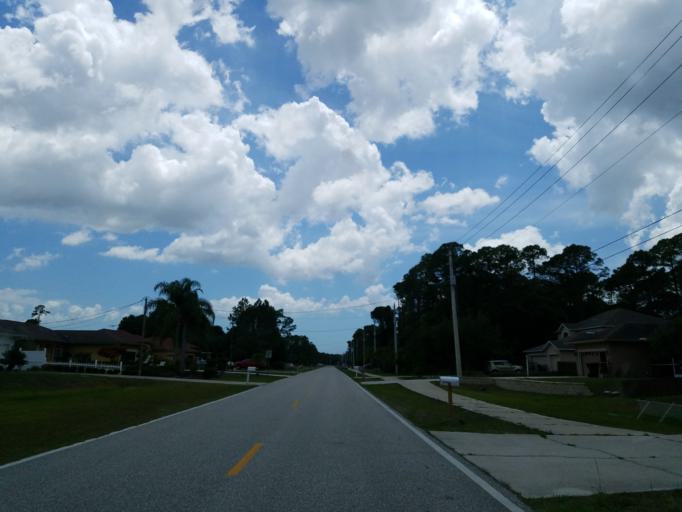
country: US
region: Florida
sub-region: Sarasota County
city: North Port
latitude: 27.0885
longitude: -82.1787
